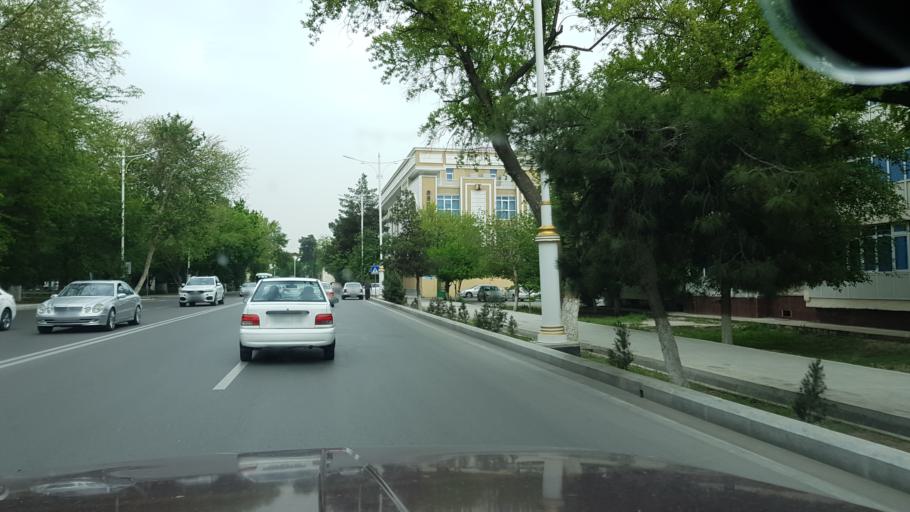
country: TM
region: Ahal
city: Ashgabat
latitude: 37.9347
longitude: 58.3923
